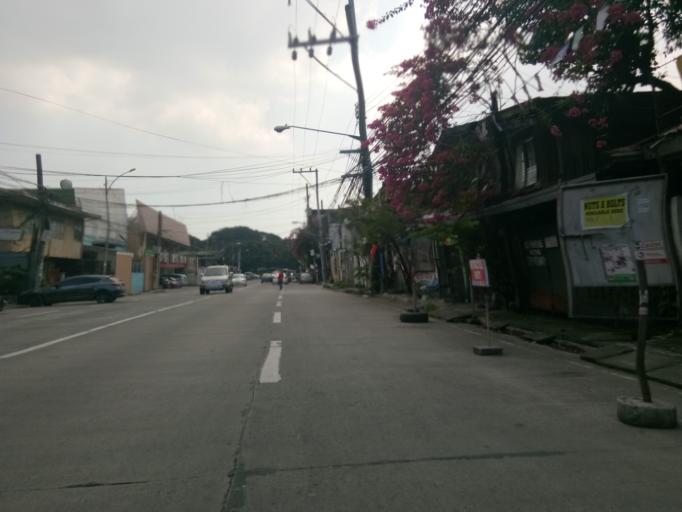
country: PH
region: Metro Manila
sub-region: Marikina
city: Calumpang
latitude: 14.6152
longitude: 121.0655
